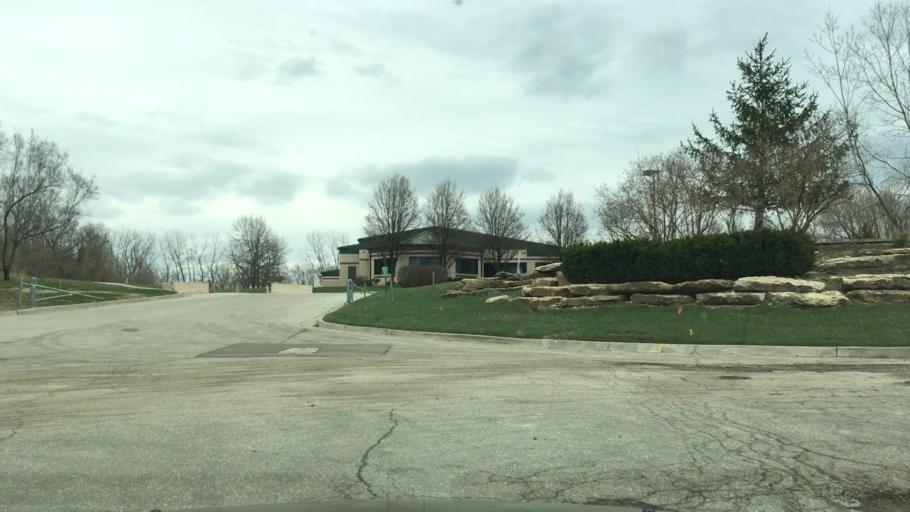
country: US
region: Missouri
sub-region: Jackson County
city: Raytown
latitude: 39.0419
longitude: -94.4756
